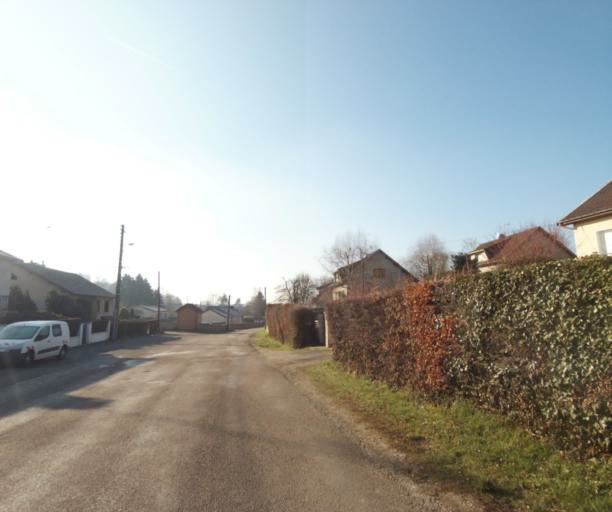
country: FR
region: Champagne-Ardenne
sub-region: Departement de la Haute-Marne
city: Wassy
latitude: 48.5001
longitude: 4.9557
